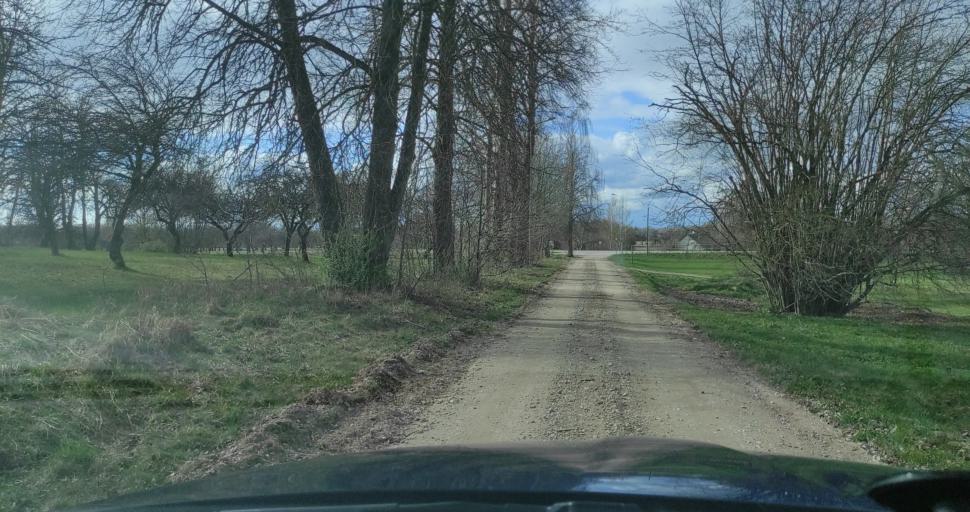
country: LV
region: Aizpute
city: Aizpute
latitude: 56.7171
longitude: 21.5855
